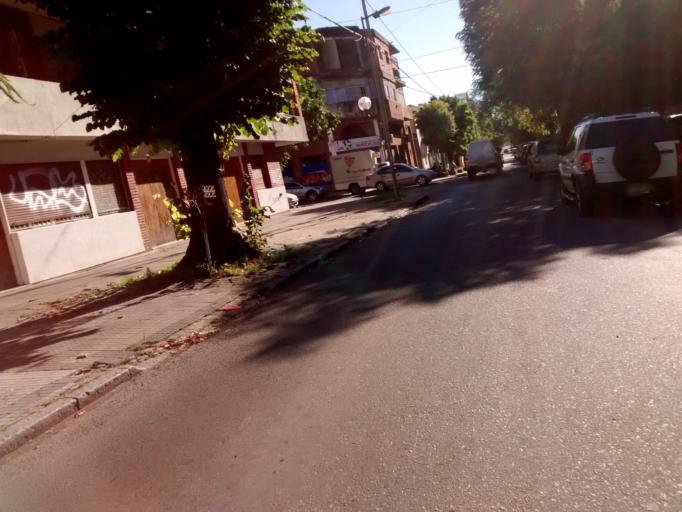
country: AR
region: Buenos Aires
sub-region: Partido de La Plata
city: La Plata
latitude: -34.9218
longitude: -57.9364
